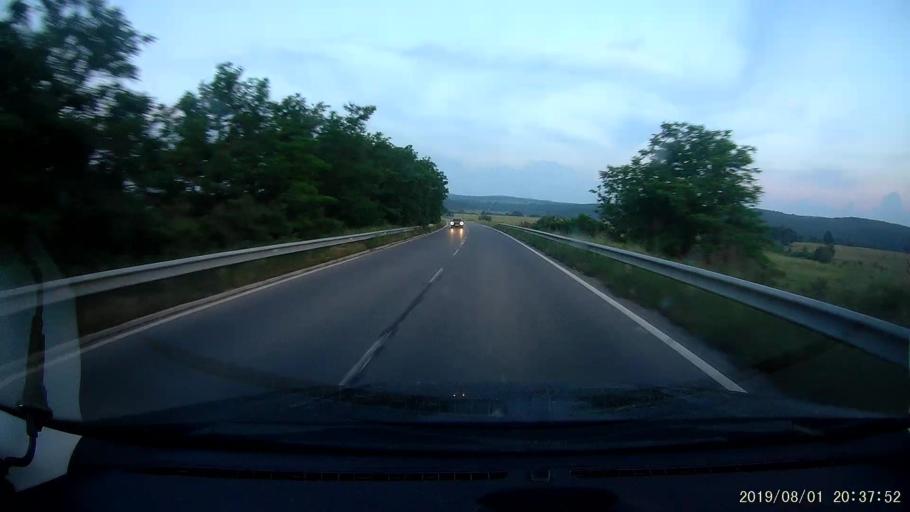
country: BG
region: Yambol
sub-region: Obshtina Elkhovo
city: Elkhovo
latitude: 42.0386
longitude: 26.5961
